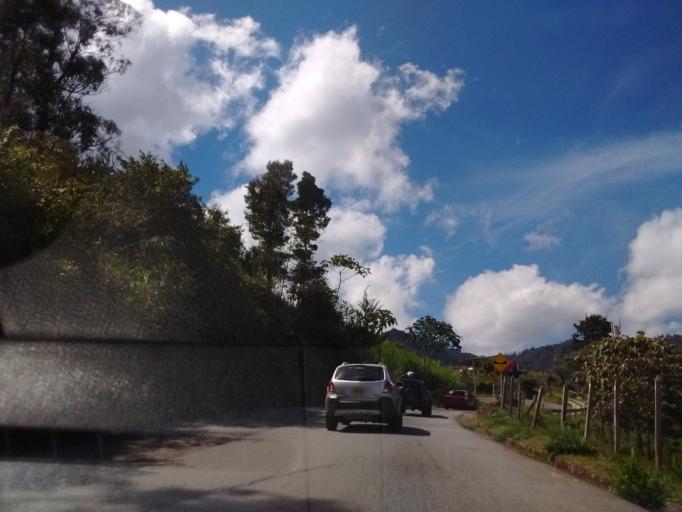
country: CO
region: Antioquia
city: Medellin
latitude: 6.2371
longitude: -75.5141
